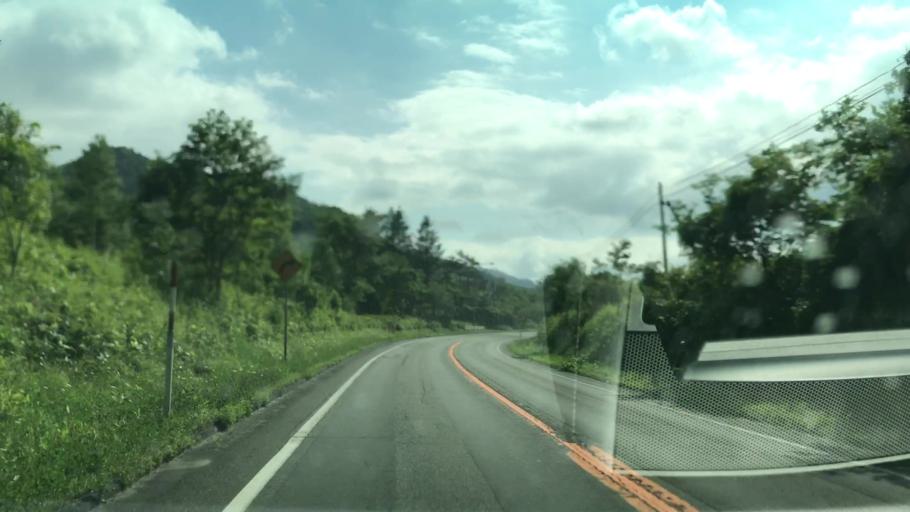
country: JP
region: Hokkaido
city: Shizunai-furukawacho
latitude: 42.8135
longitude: 142.4190
